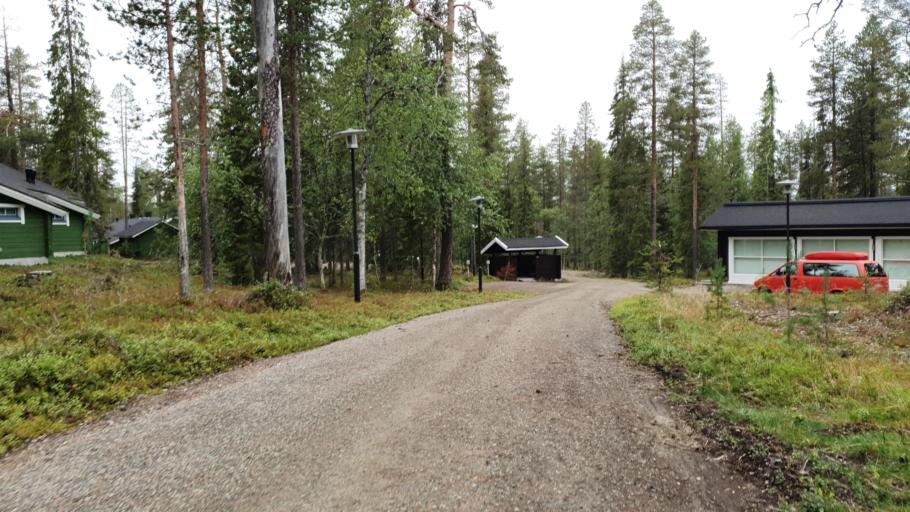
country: FI
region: Lapland
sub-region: Tunturi-Lappi
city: Kolari
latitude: 67.5978
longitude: 24.1923
